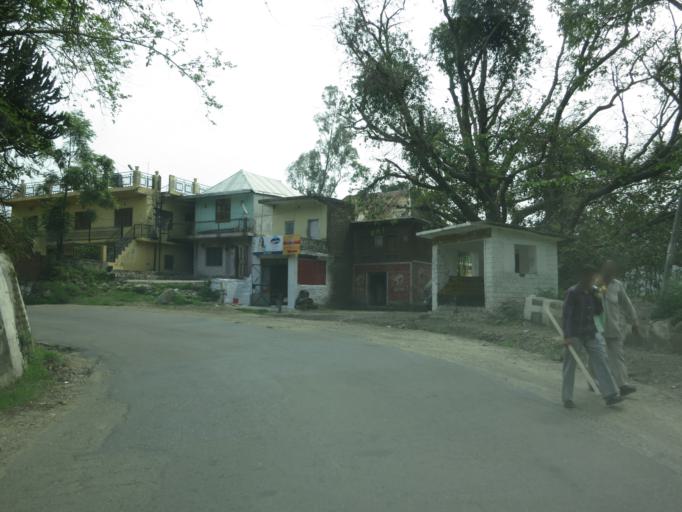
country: IN
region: Himachal Pradesh
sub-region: Solan
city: Arki
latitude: 31.2550
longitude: 76.8743
